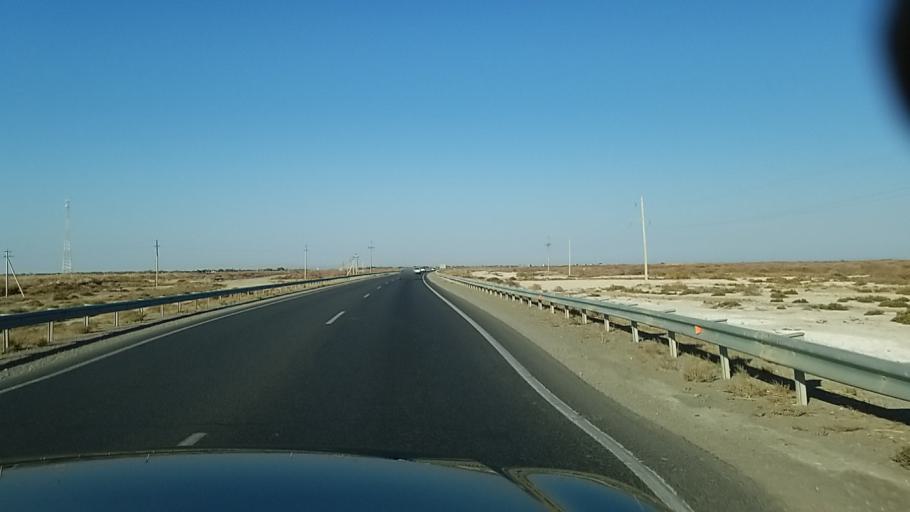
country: KZ
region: Qyzylorda
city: Terenozek
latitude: 44.8944
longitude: 65.0100
